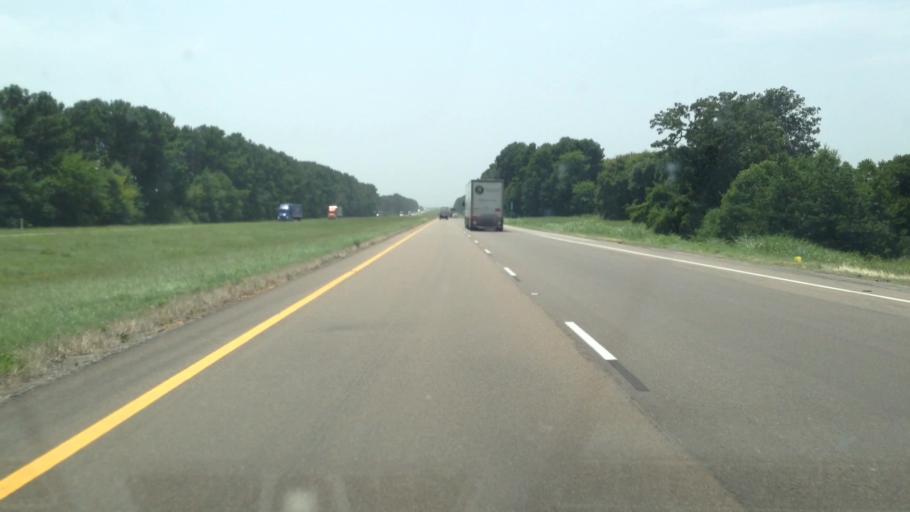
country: US
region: Texas
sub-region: Morris County
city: Naples
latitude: 33.2939
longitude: -94.7441
